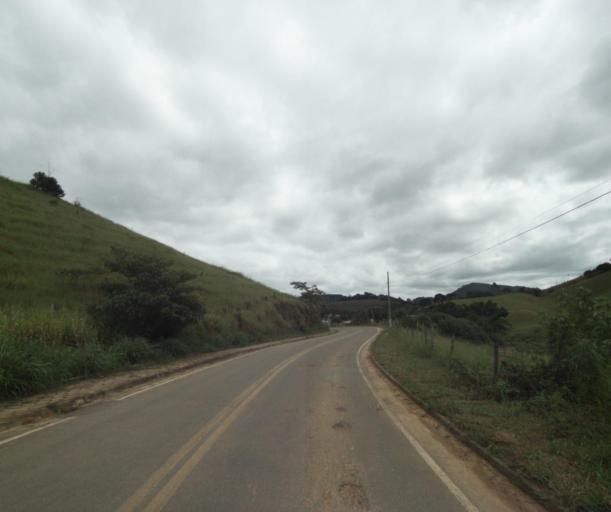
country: BR
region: Espirito Santo
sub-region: Irupi
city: Irupi
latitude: -20.3517
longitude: -41.6317
